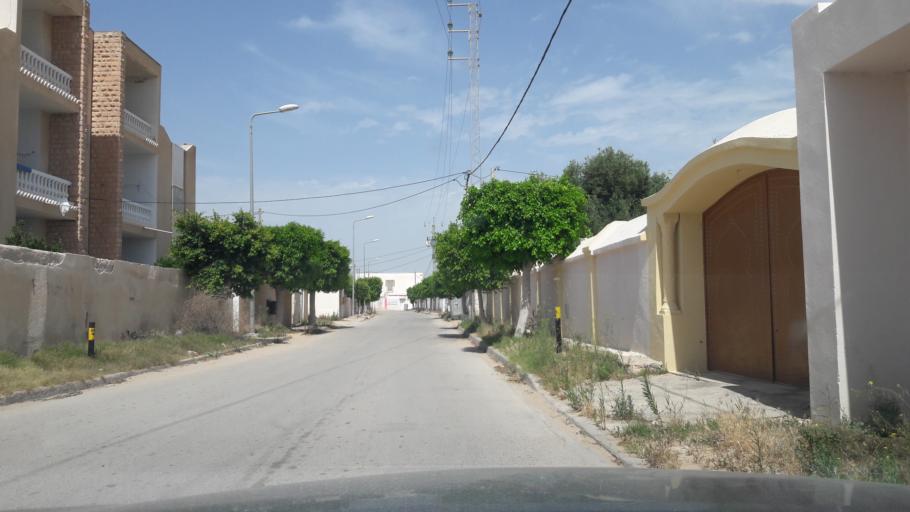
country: TN
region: Safaqis
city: Al Qarmadah
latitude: 34.7795
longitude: 10.7630
